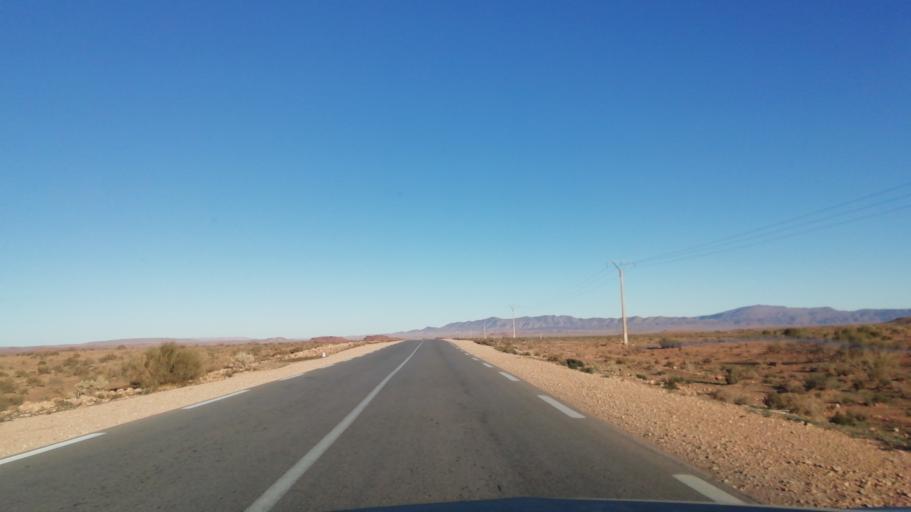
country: DZ
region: El Bayadh
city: El Abiodh Sidi Cheikh
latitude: 33.1672
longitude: 0.4692
